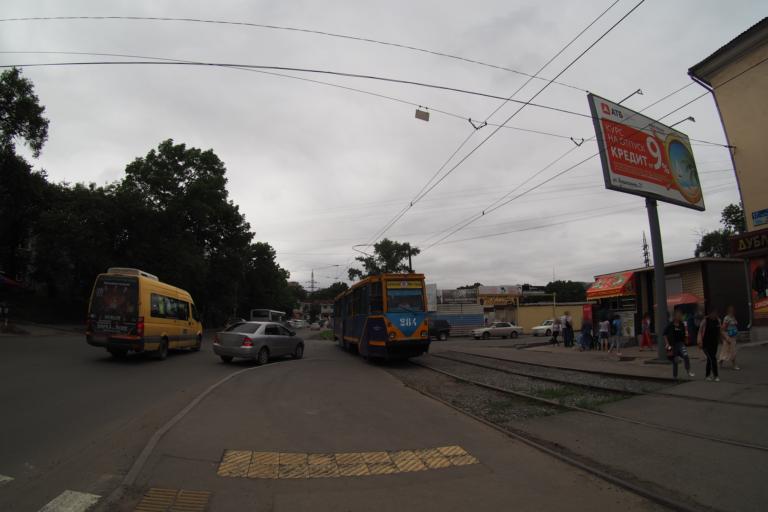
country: RU
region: Primorskiy
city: Vladivostok
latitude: 43.1013
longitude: 131.9447
